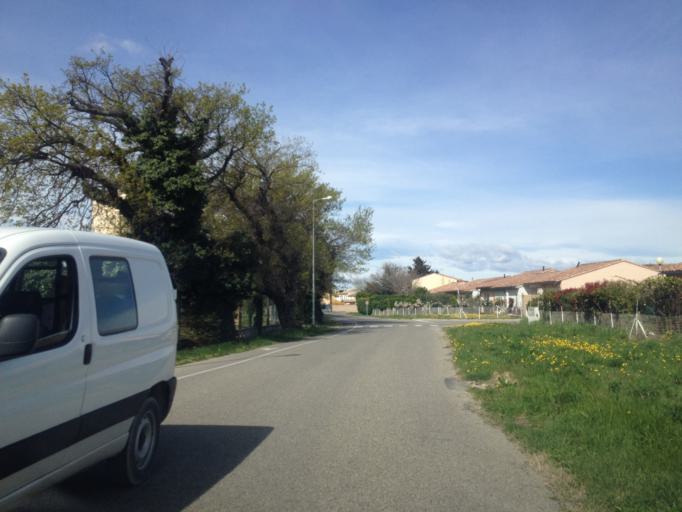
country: FR
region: Provence-Alpes-Cote d'Azur
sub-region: Departement du Vaucluse
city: Camaret-sur-Aigues
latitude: 44.1666
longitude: 4.8659
